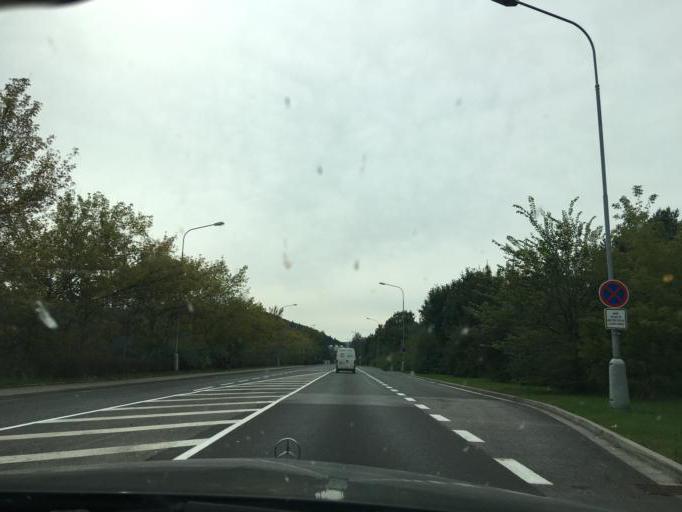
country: CZ
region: Kralovehradecky
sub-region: Okres Nachod
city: Nachod
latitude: 50.4232
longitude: 16.1877
